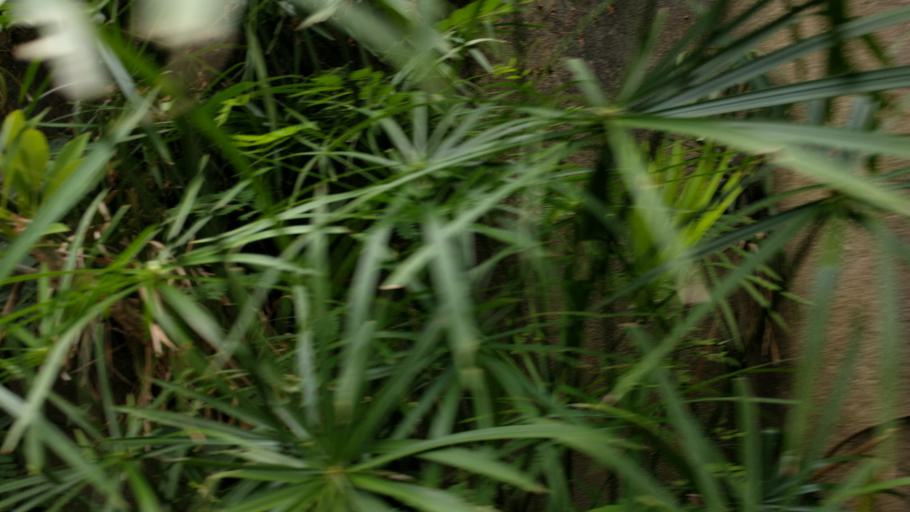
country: ID
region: Bali
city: Kuta
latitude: -8.6758
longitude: 115.1499
